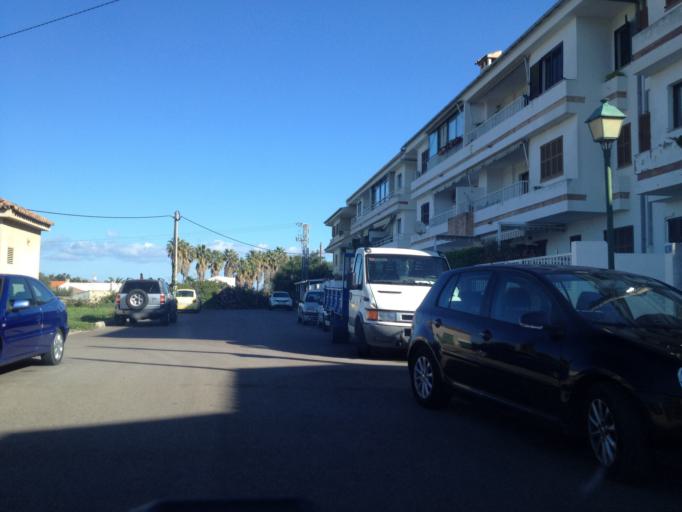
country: ES
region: Balearic Islands
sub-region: Illes Balears
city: Alcudia
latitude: 39.8535
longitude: 3.1136
